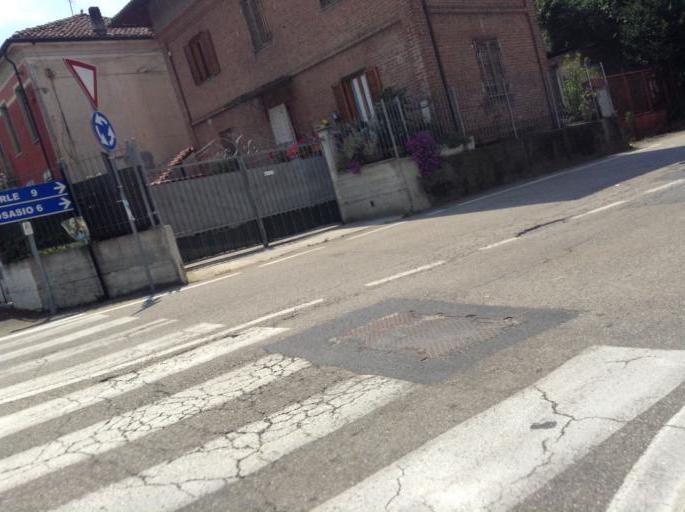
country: IT
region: Piedmont
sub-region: Provincia di Torino
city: Carignano
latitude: 44.8964
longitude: 7.6698
